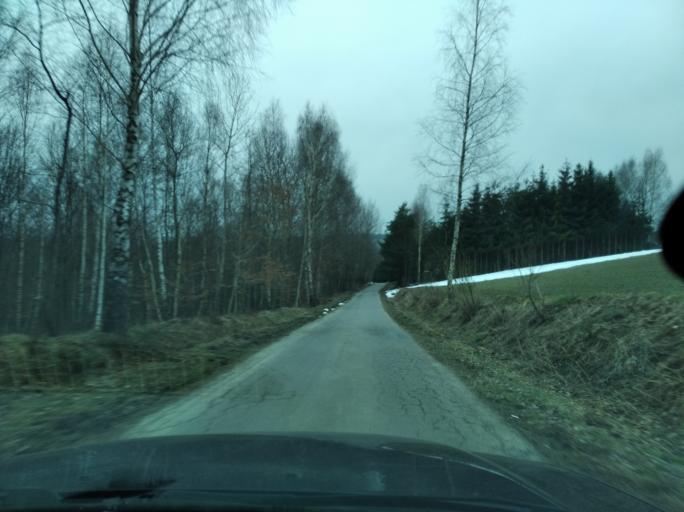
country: PL
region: Subcarpathian Voivodeship
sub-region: Powiat rzeszowski
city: Chmielnik
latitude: 49.9858
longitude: 22.1355
